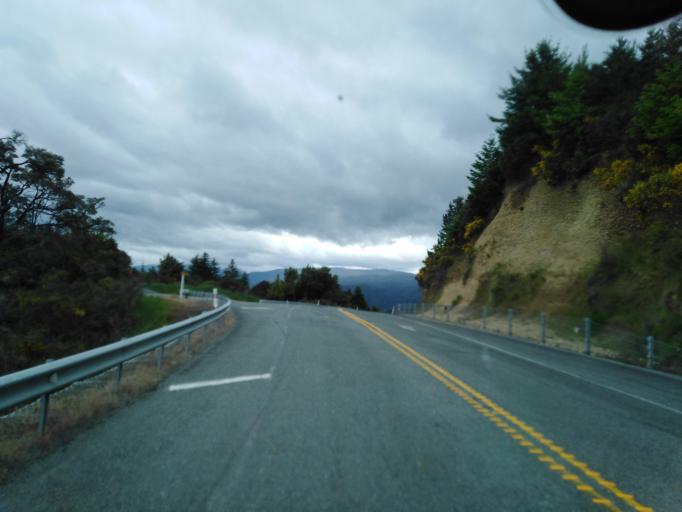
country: NZ
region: Tasman
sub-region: Tasman District
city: Wakefield
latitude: -41.6290
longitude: 172.7204
